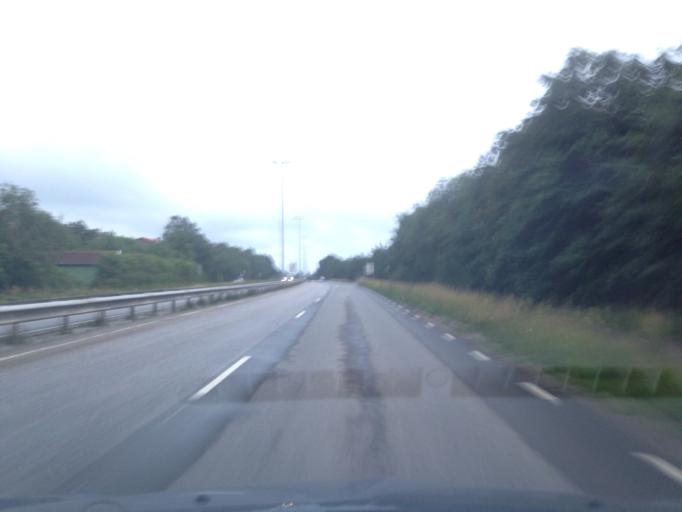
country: SE
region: Halland
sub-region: Varbergs Kommun
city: Varberg
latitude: 57.1206
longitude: 12.2617
